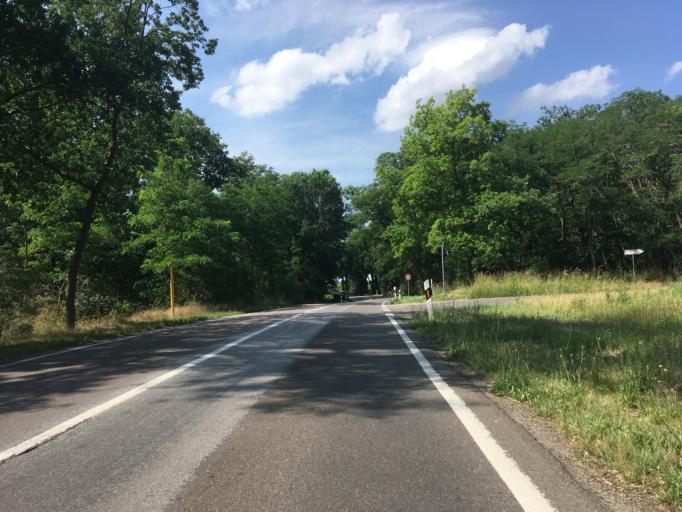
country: DE
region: Saxony-Anhalt
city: Quellendorf
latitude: 51.7851
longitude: 12.1529
